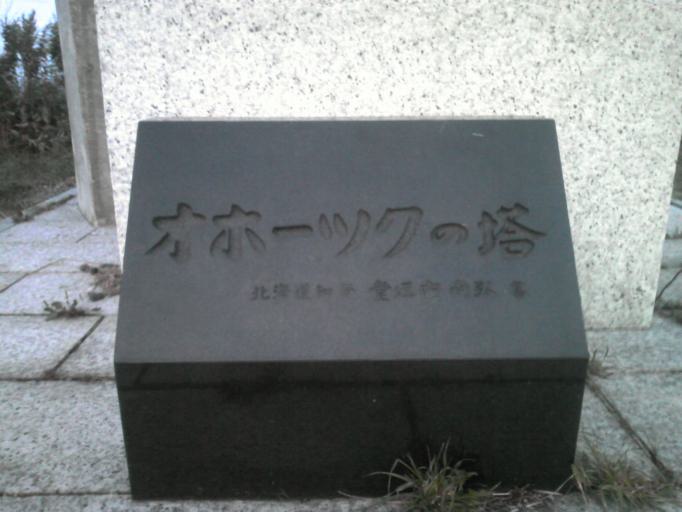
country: JP
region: Hokkaido
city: Abashiri
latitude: 44.1112
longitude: 144.2415
